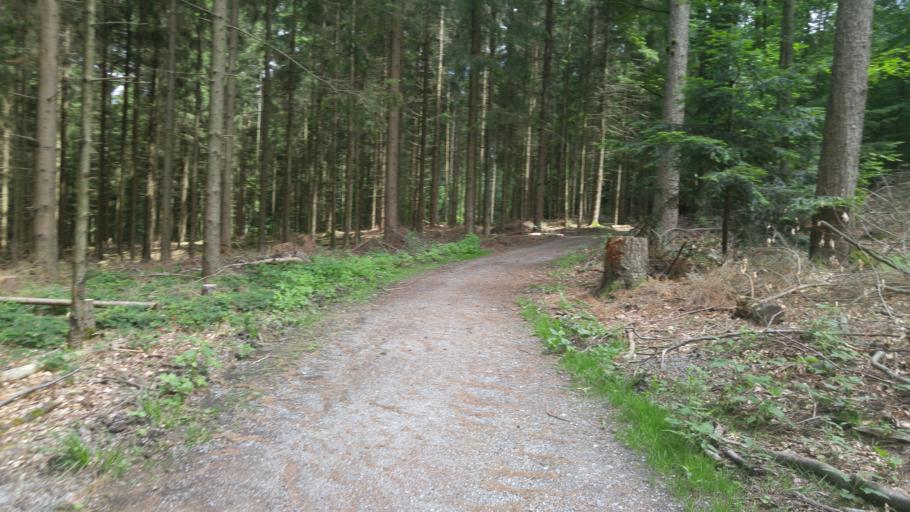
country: DE
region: Baden-Wuerttemberg
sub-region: Regierungsbezirk Stuttgart
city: Wustenrot
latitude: 49.0798
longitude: 9.4459
